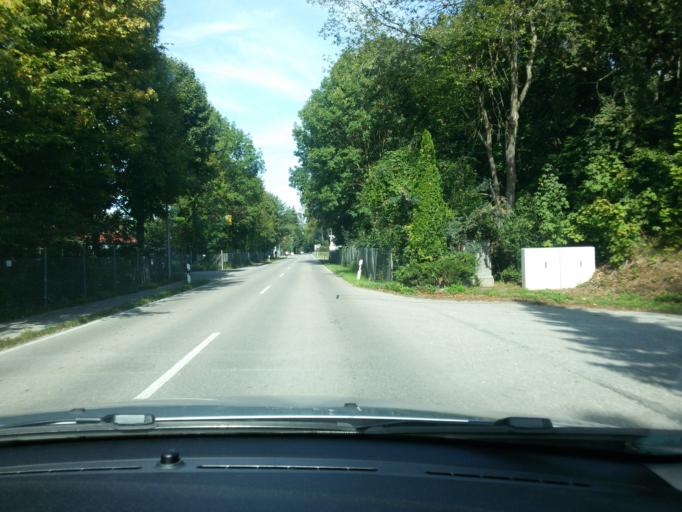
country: DE
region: Bavaria
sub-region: Swabia
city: Wehringen
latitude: 48.2645
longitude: 10.7900
